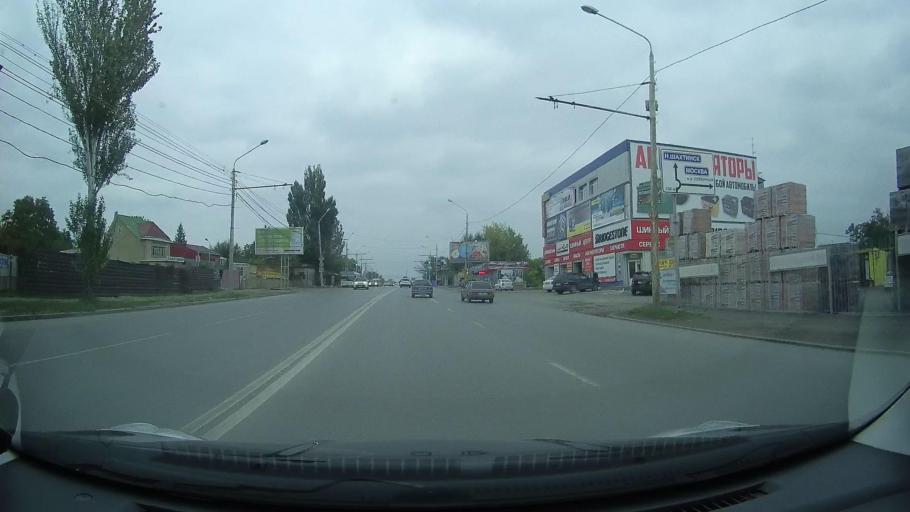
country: RU
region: Rostov
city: Severnyy
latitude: 47.2797
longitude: 39.6841
